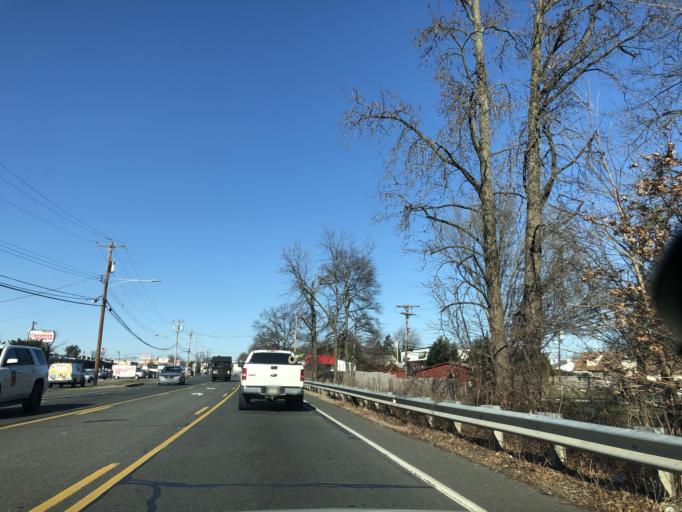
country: US
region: Pennsylvania
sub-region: Bucks County
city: Hulmeville
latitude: 40.1311
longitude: -74.8833
